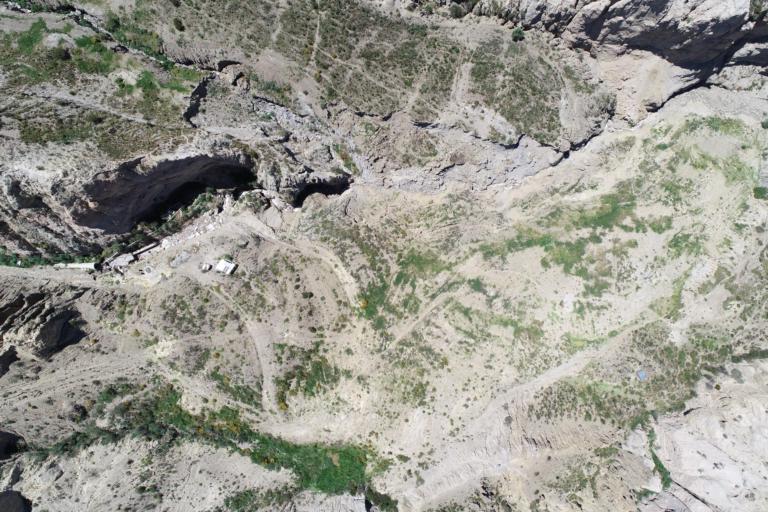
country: BO
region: La Paz
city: La Paz
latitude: -16.5165
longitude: -68.0996
